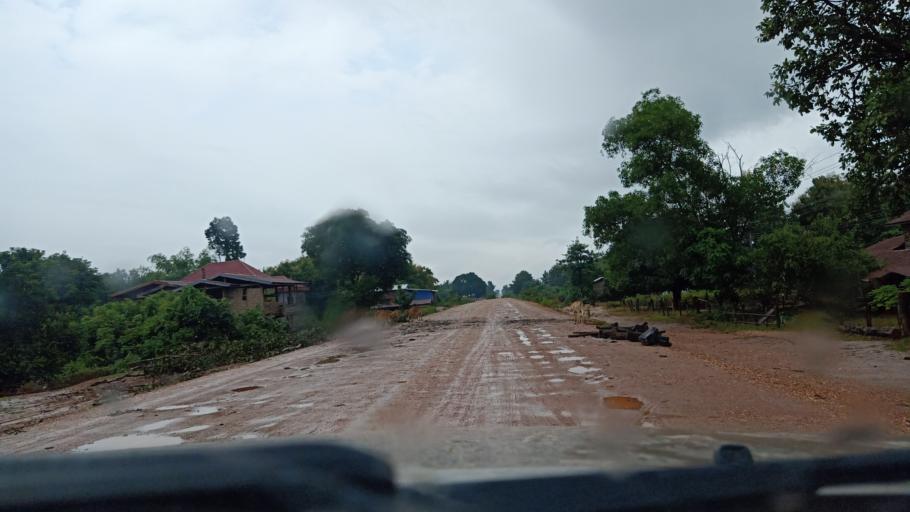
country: LA
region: Attapu
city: Attapu
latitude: 14.7117
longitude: 106.6608
